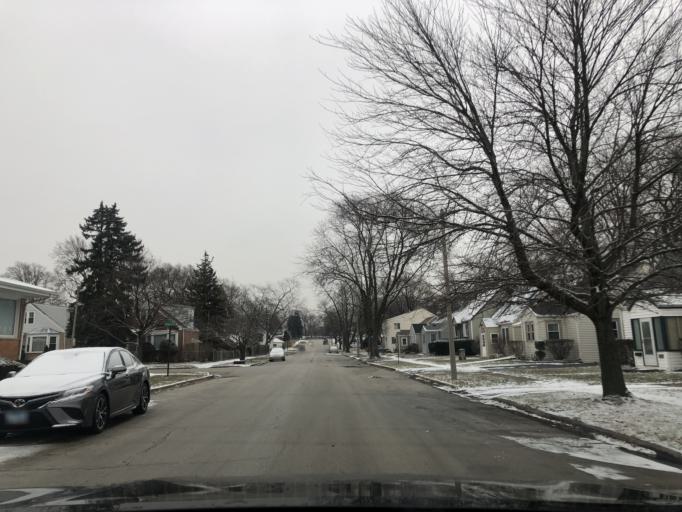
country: US
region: Illinois
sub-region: Cook County
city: Evergreen Park
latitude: 41.7317
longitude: -87.6917
